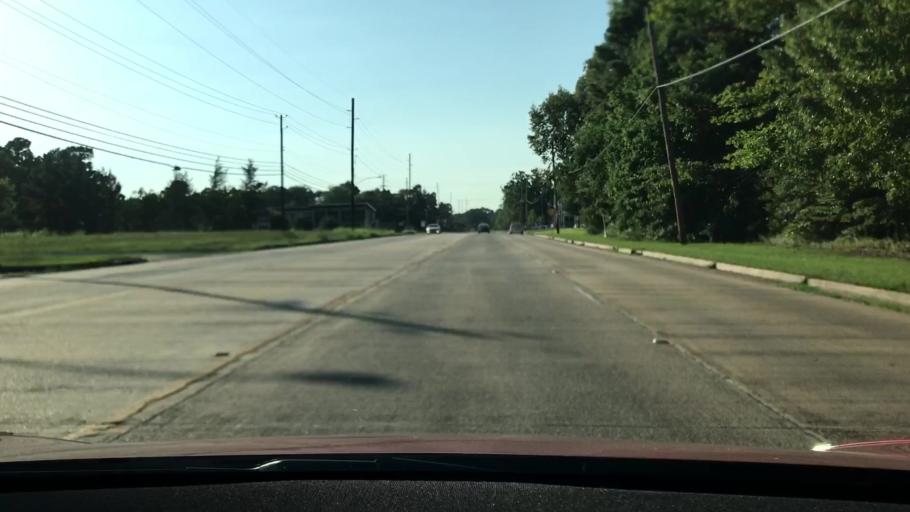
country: US
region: Louisiana
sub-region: Bossier Parish
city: Bossier City
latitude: 32.4262
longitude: -93.7407
